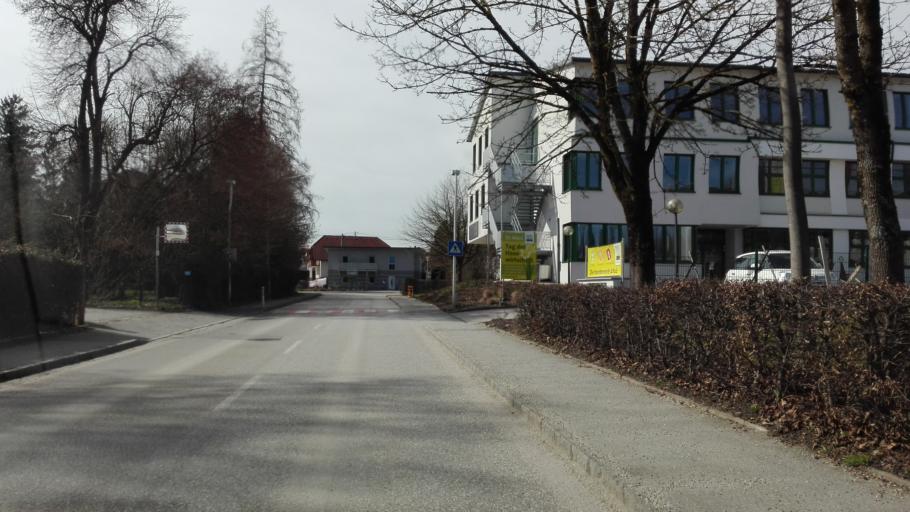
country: AT
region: Upper Austria
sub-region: Politischer Bezirk Scharding
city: Sankt Marienkirchen bei Schaerding
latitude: 48.3728
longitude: 13.5725
